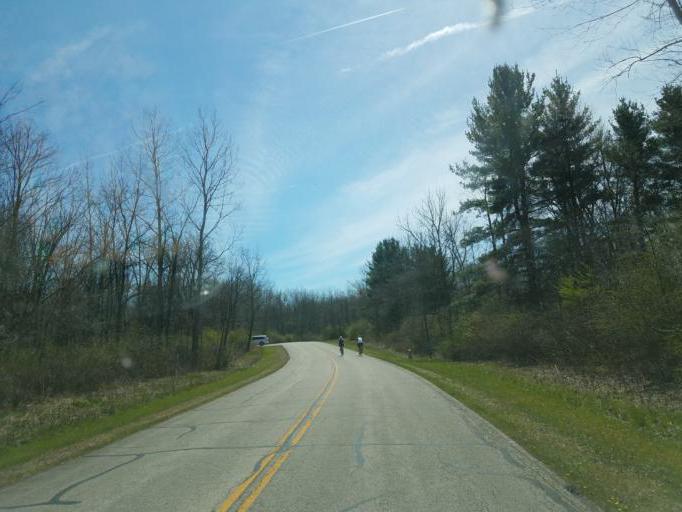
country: US
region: Ohio
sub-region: Delaware County
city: Delaware
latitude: 40.3920
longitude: -83.0669
